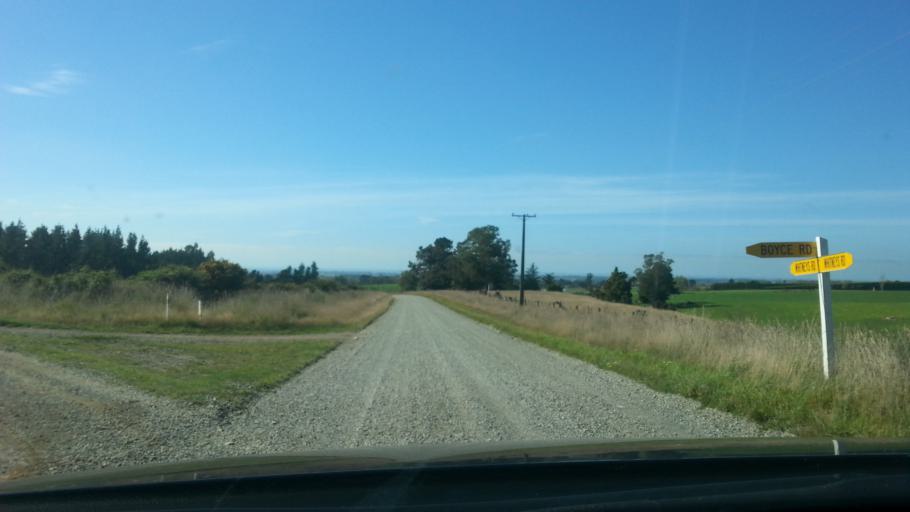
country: NZ
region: Otago
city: Oamaru
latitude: -44.7119
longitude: 171.0089
